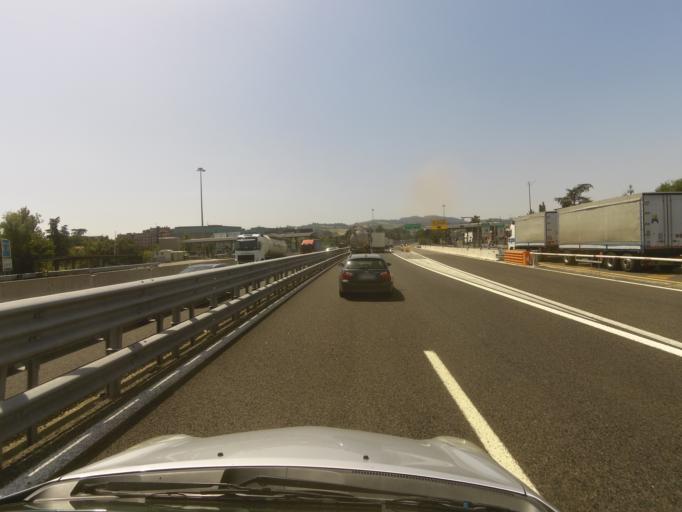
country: IT
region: Emilia-Romagna
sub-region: Provincia di Bologna
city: Casalecchio di Reno
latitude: 44.4894
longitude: 11.2689
